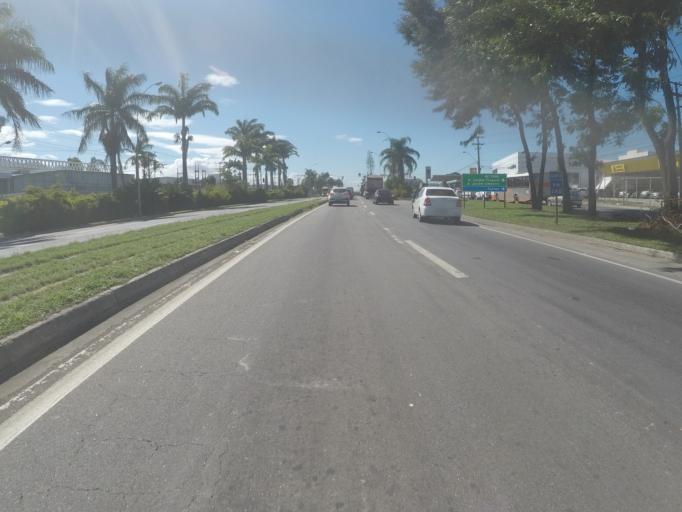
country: BR
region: Espirito Santo
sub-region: Serra
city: Serra
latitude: -20.2084
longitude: -40.2694
